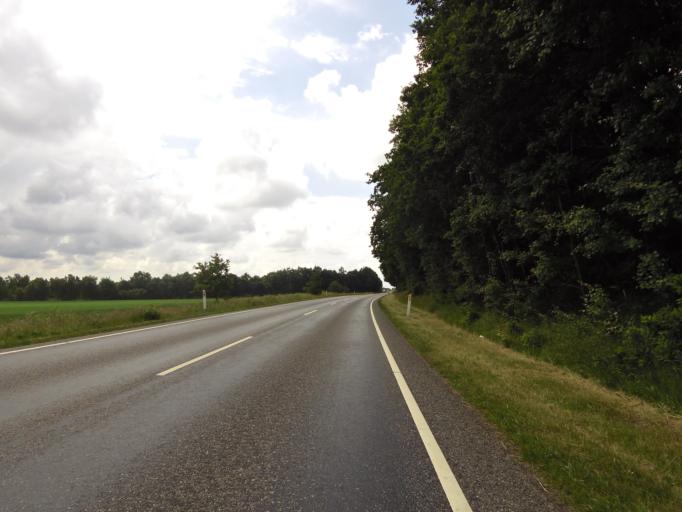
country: DK
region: South Denmark
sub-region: Haderslev Kommune
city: Gram
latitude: 55.2309
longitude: 8.9311
